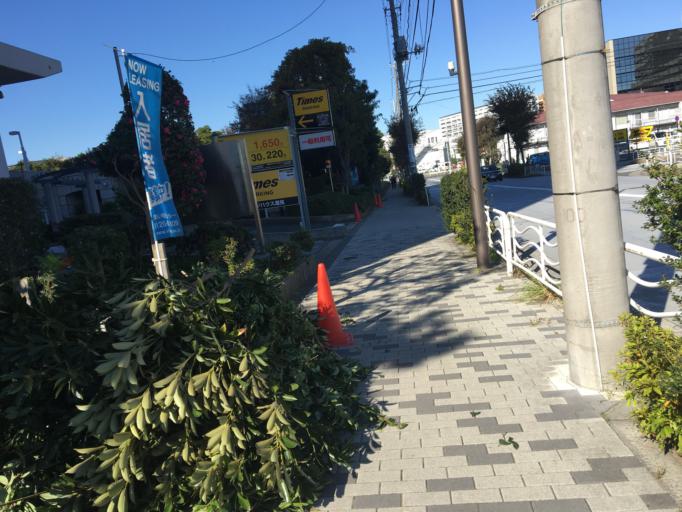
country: JP
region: Tokyo
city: Urayasu
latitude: 35.6558
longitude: 139.8161
